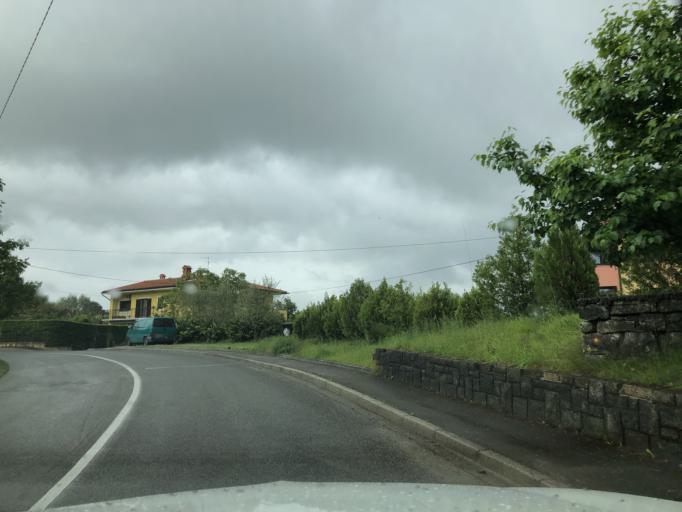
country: SI
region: Koper-Capodistria
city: Prade
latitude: 45.5006
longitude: 13.7827
